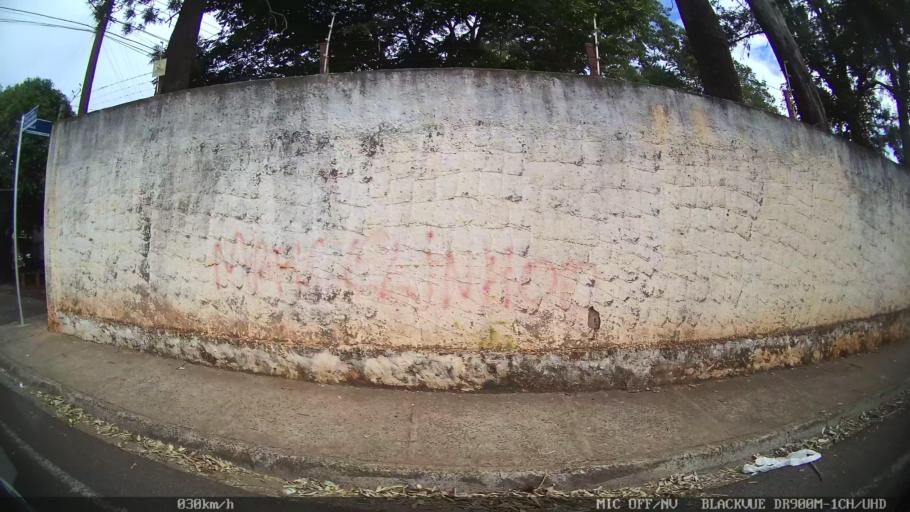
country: BR
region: Sao Paulo
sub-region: Catanduva
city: Catanduva
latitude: -21.1521
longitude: -48.9636
